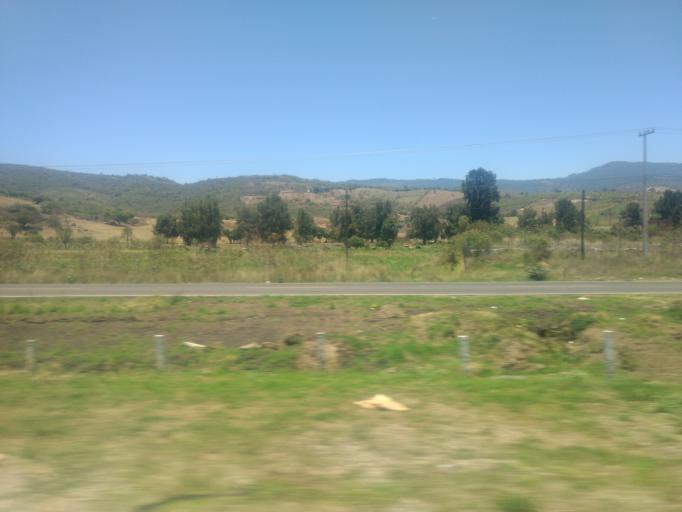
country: MX
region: Jalisco
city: San Andres Ixtlan
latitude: 19.8289
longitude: -103.4965
